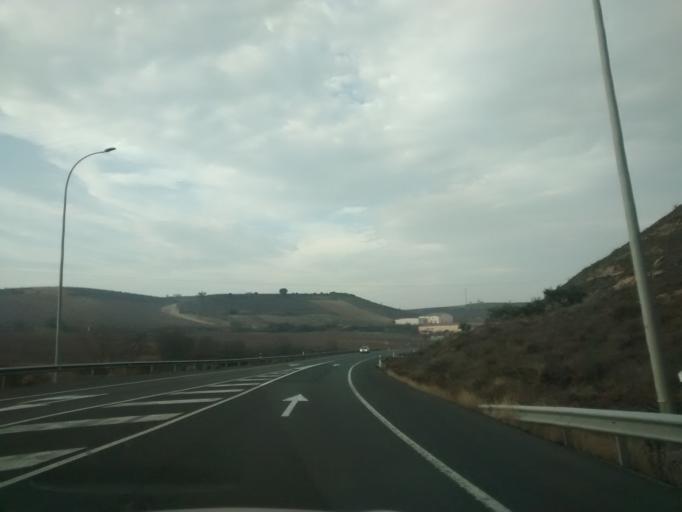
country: ES
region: La Rioja
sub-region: Provincia de La Rioja
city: Cenicero
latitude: 42.4721
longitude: -2.6411
